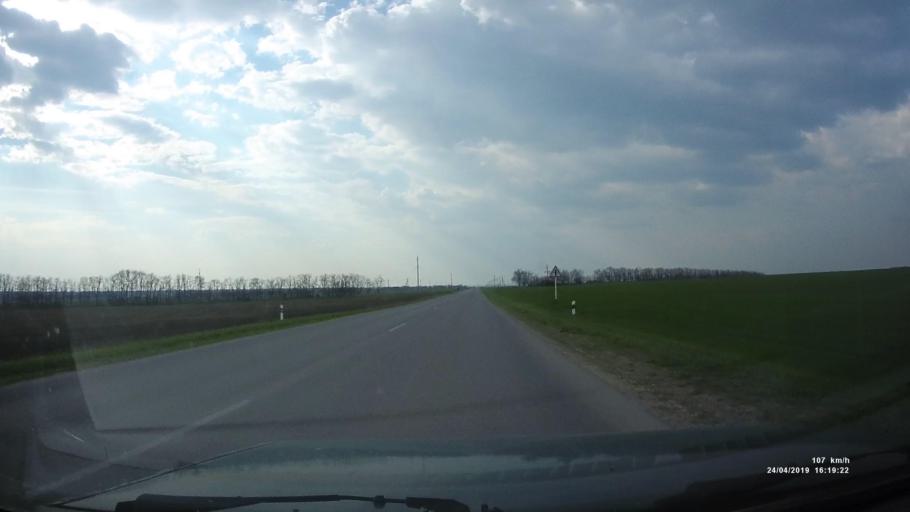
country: RU
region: Rostov
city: Sovetskoye
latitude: 46.7810
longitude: 42.0971
